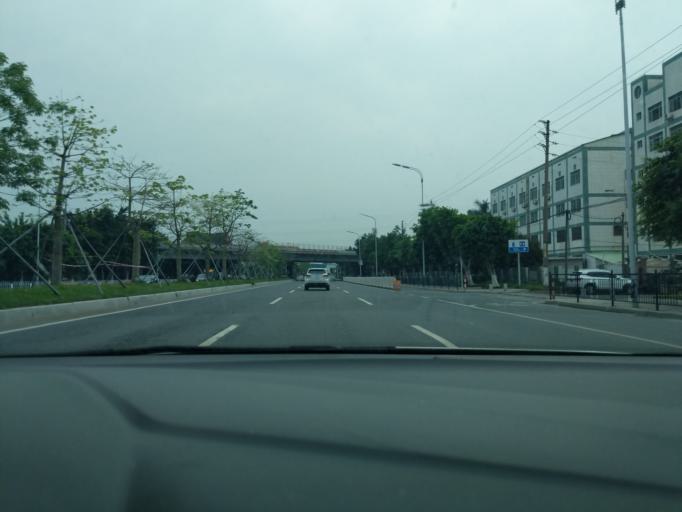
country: CN
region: Guangdong
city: Huangge
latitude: 22.8592
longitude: 113.4863
